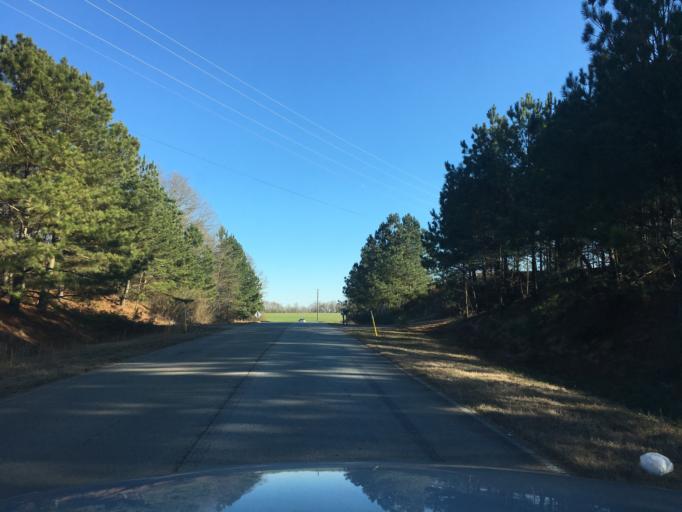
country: US
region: Georgia
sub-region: Carroll County
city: Carrollton
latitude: 33.4406
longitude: -85.1302
